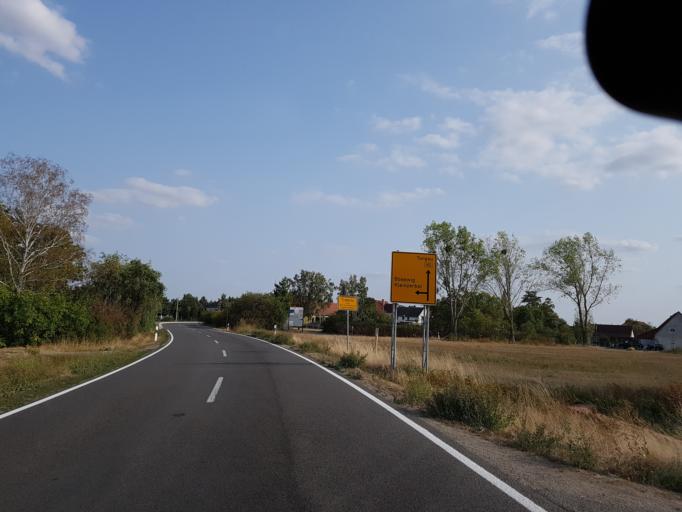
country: DE
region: Saxony-Anhalt
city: Pretzsch
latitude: 51.7568
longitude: 12.7499
